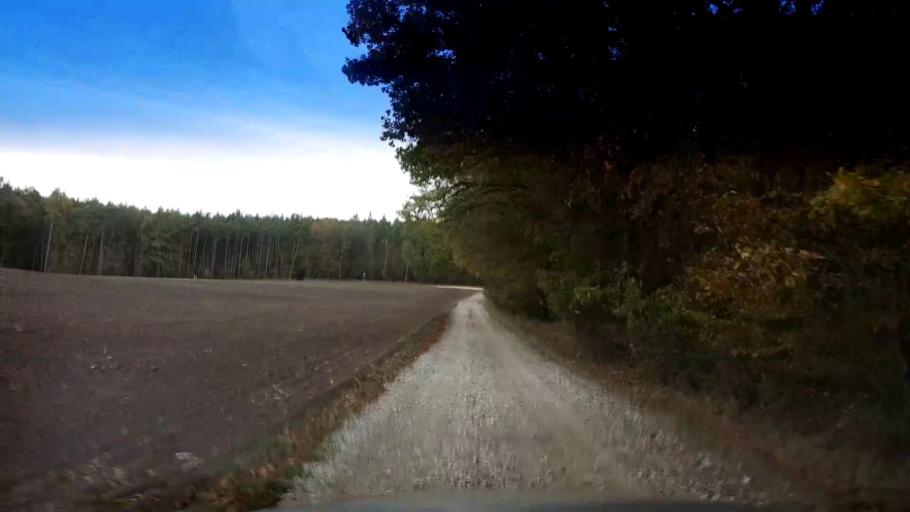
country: DE
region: Bavaria
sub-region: Upper Franconia
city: Priesendorf
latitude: 49.9184
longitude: 10.7203
